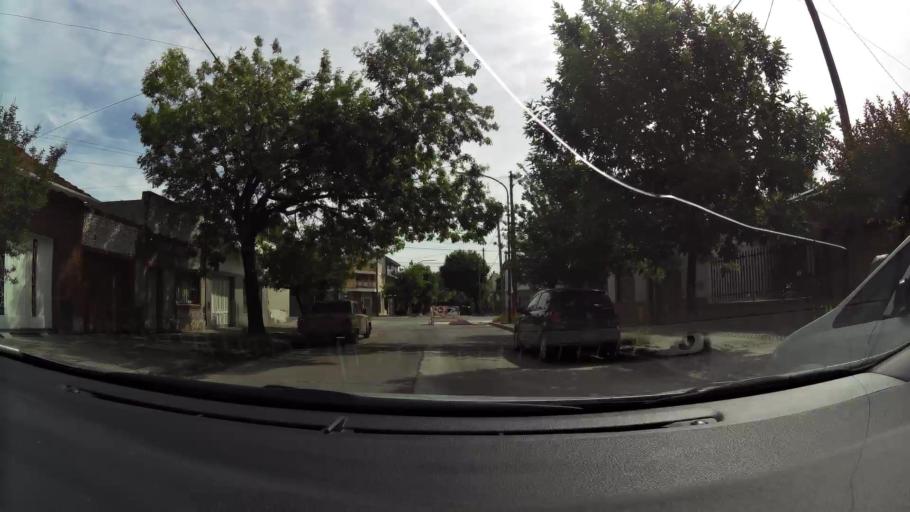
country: AR
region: Buenos Aires F.D.
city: Villa Lugano
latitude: -34.6606
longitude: -58.4326
